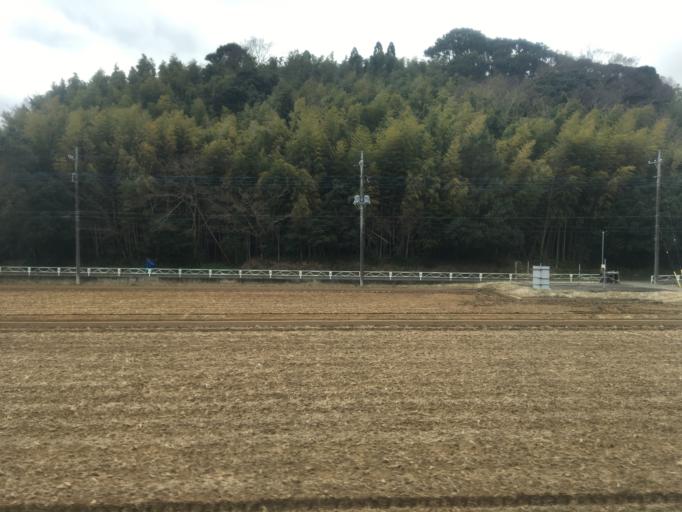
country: JP
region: Ibaraki
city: Ryugasaki
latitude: 35.8325
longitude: 140.1904
